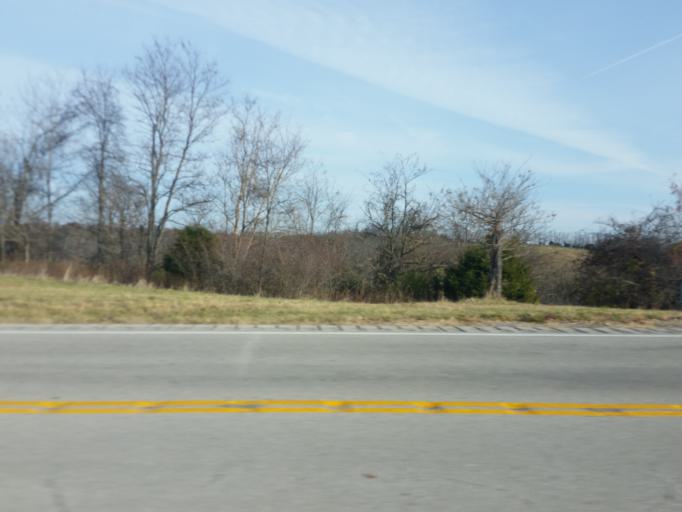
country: US
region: Kentucky
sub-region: Harrison County
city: Cynthiana
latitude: 38.5211
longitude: -84.2880
